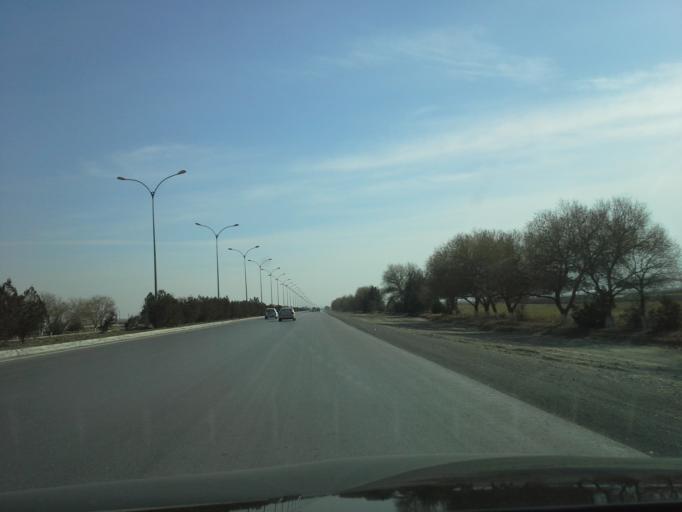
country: TM
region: Ahal
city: Abadan
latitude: 38.1329
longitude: 58.0184
